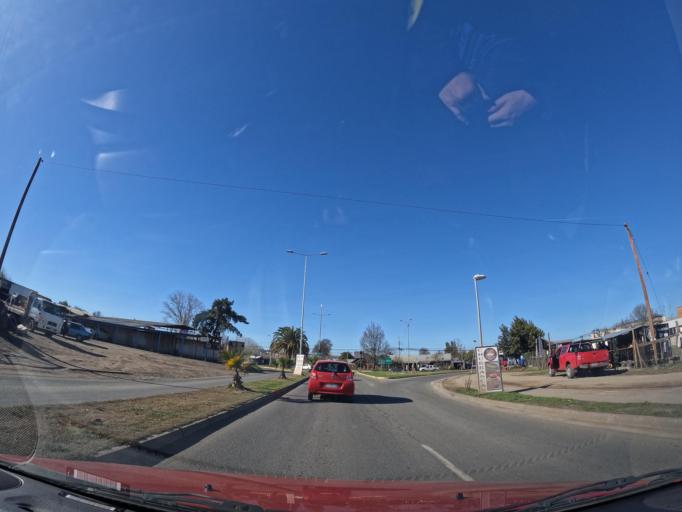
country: CL
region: Maule
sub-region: Provincia de Cauquenes
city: Cauquenes
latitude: -35.9616
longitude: -72.3133
